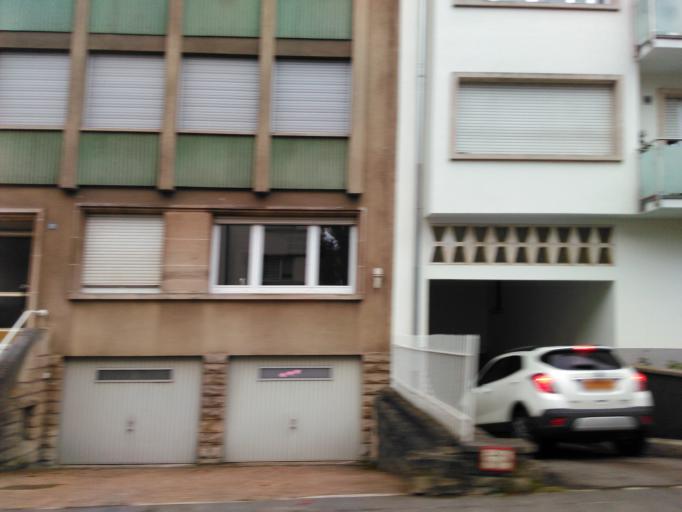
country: LU
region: Luxembourg
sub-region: Canton de Luxembourg
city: Luxembourg
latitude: 49.6198
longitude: 6.1158
